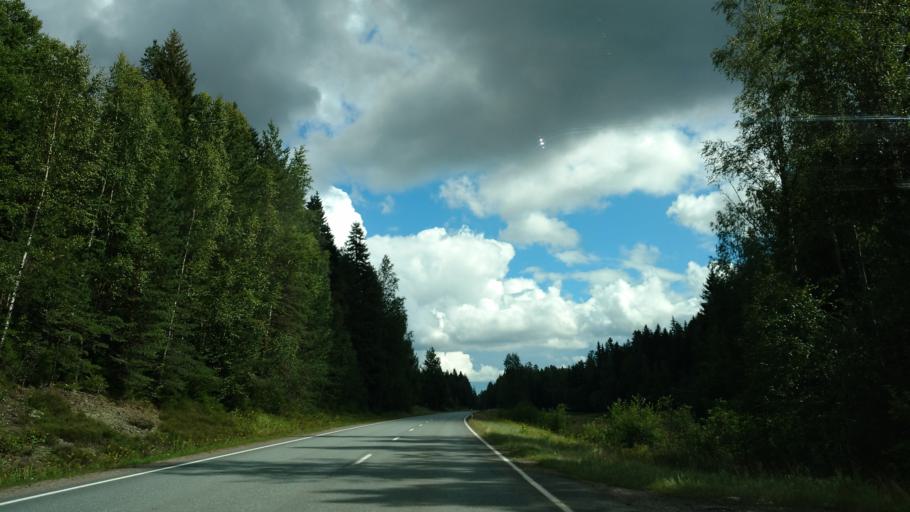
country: FI
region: Varsinais-Suomi
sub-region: Salo
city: Kisko
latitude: 60.2465
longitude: 23.5185
